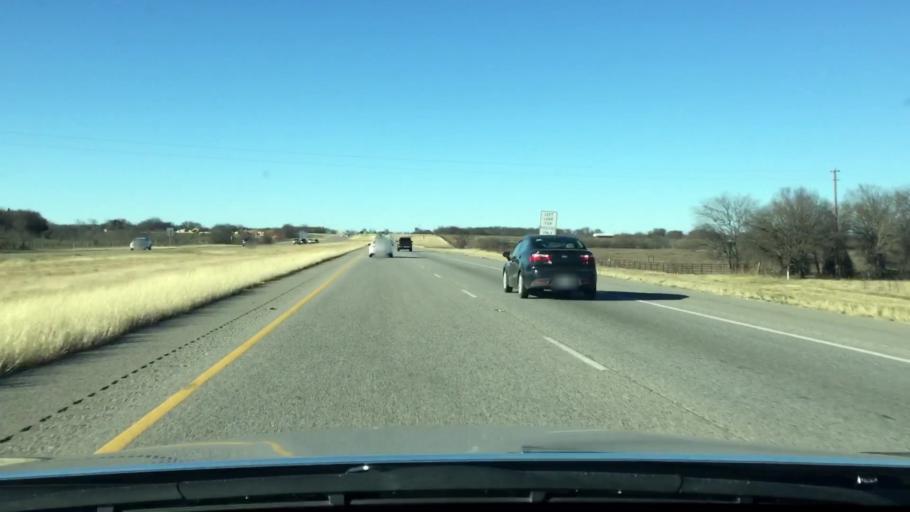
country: US
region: Texas
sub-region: Johnson County
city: Grandview
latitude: 32.2442
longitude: -97.1586
